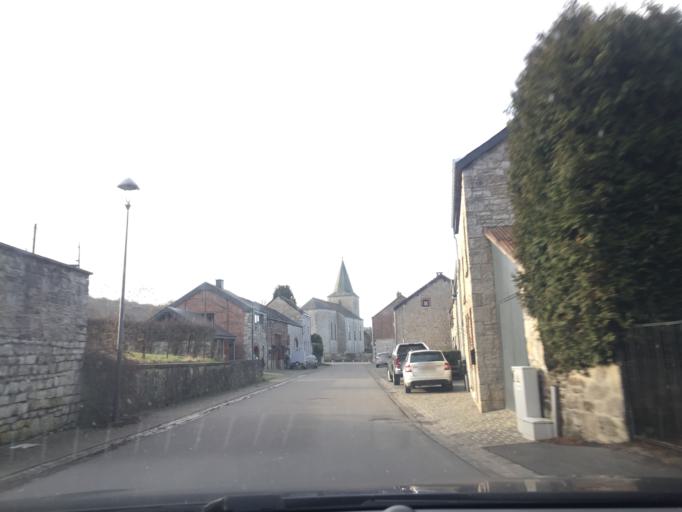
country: BE
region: Wallonia
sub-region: Province du Luxembourg
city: Hotton
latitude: 50.2864
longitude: 5.4815
